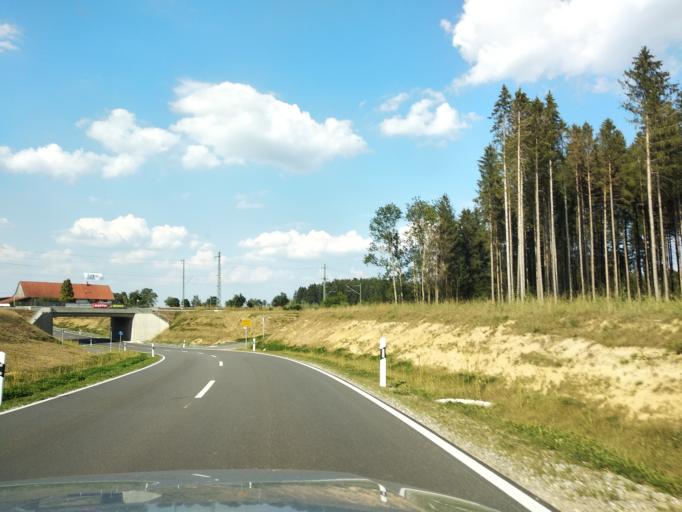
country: DE
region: Bavaria
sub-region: Swabia
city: Holzgunz
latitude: 48.0143
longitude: 10.2750
